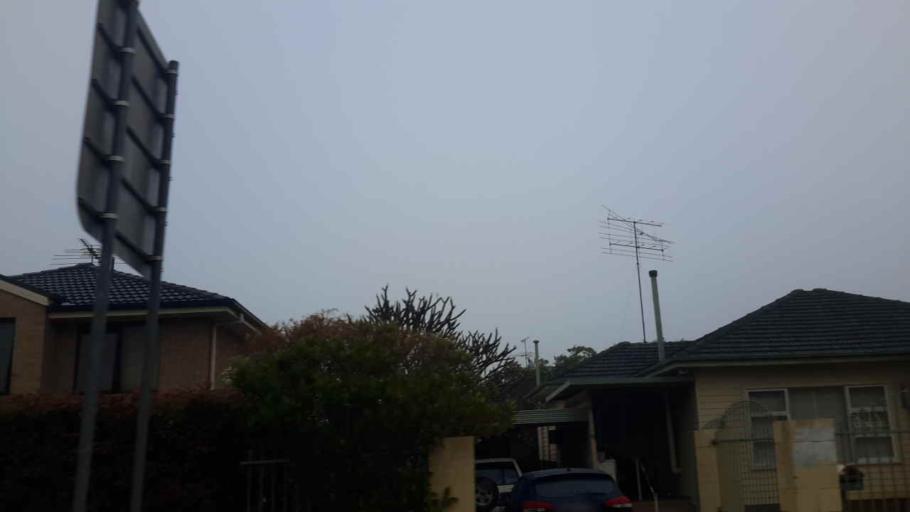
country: AU
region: New South Wales
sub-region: Penrith Municipality
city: Kingswood Park
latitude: -33.7616
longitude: 150.7104
